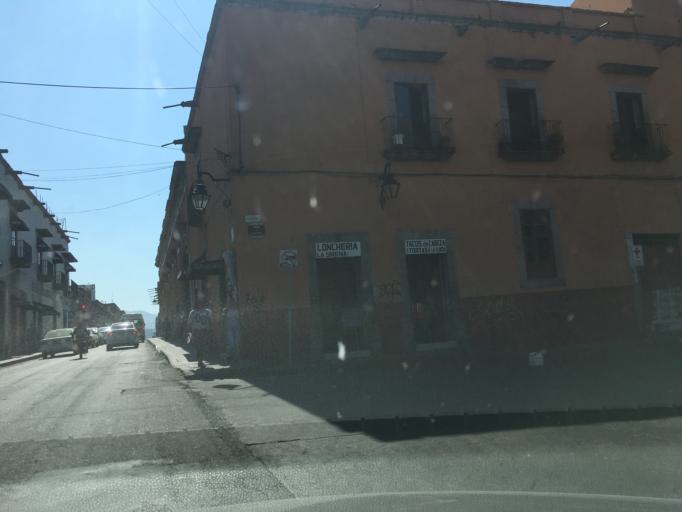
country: MX
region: Michoacan
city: Morelia
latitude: 19.7053
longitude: -101.1915
